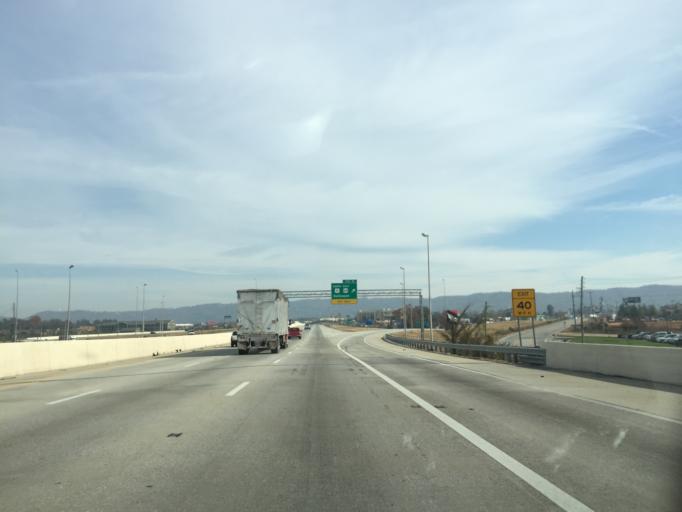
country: US
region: Tennessee
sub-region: Hamilton County
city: Collegedale
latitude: 35.0847
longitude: -85.0720
